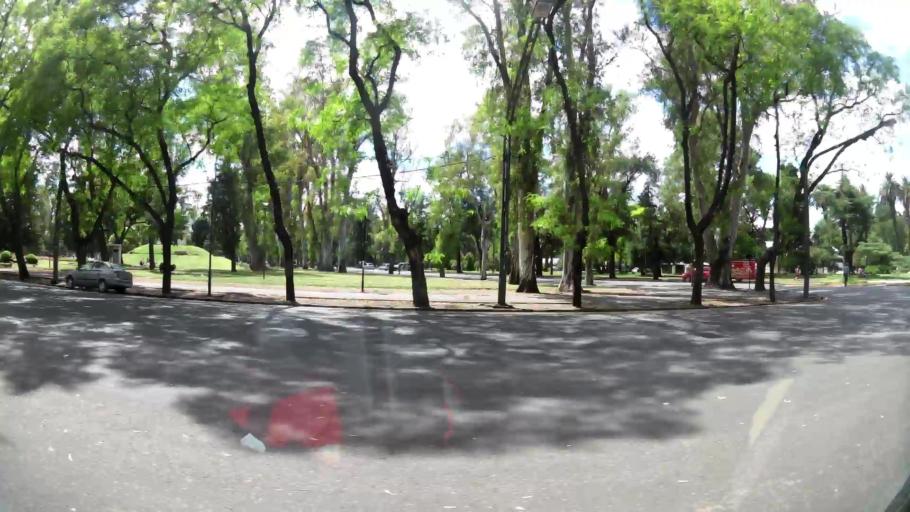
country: AR
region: Santa Fe
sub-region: Departamento de Rosario
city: Rosario
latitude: -32.9615
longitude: -60.6578
